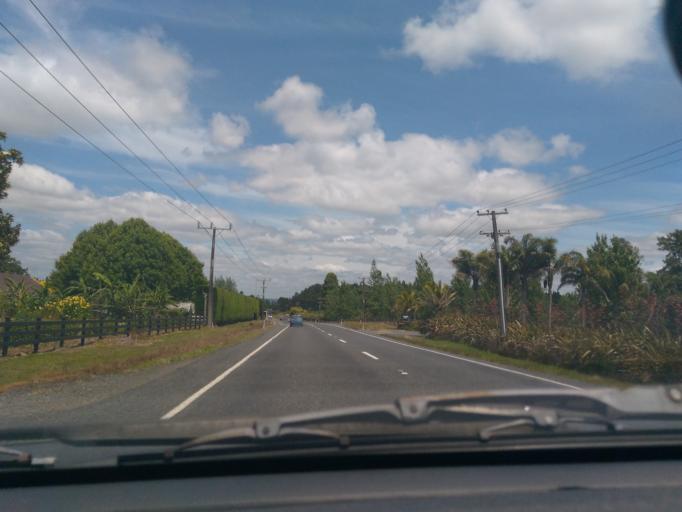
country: NZ
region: Northland
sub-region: Far North District
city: Kerikeri
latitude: -35.1640
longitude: 173.8933
